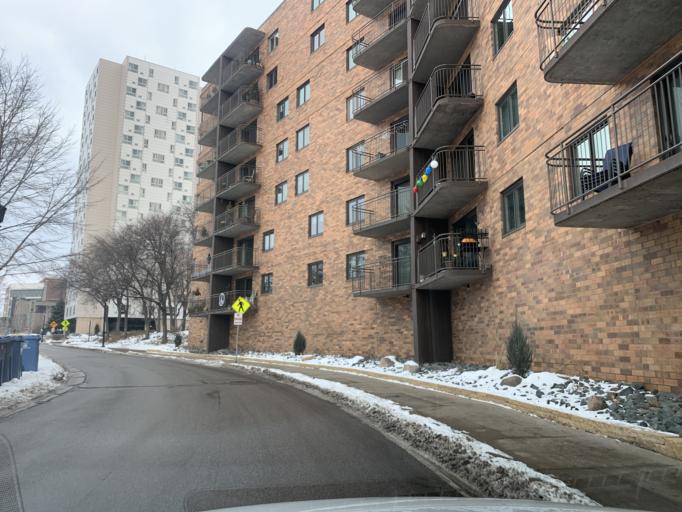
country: US
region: Minnesota
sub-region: Hennepin County
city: Minneapolis
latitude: 44.9701
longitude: -93.2818
